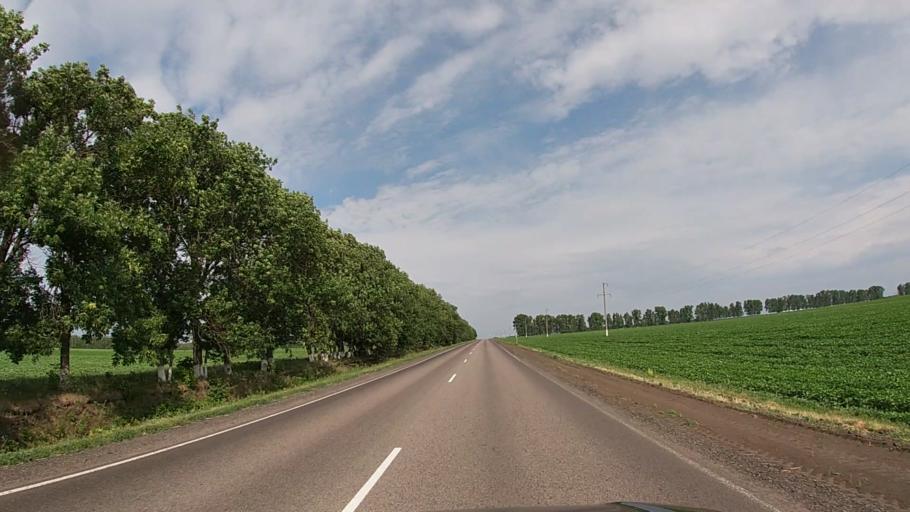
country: RU
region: Belgorod
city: Krasnaya Yaruga
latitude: 50.8037
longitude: 35.5521
